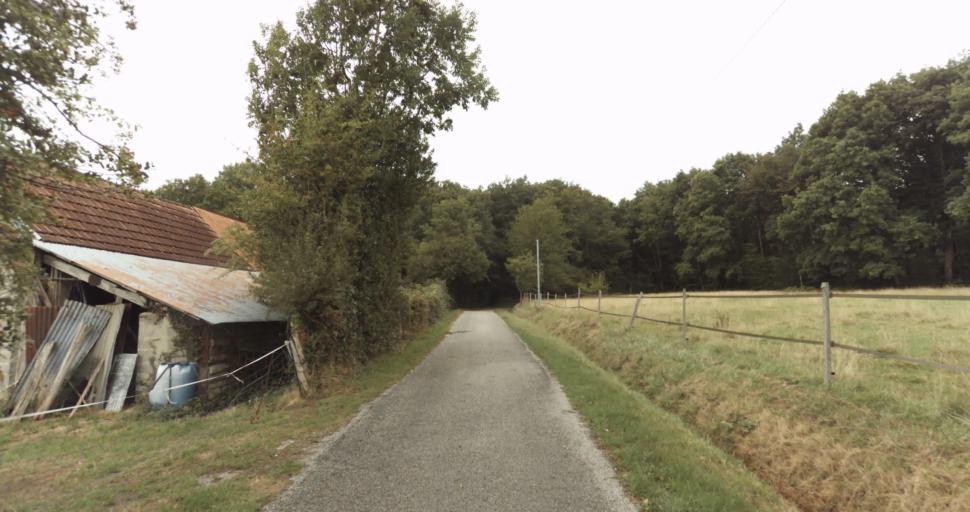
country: FR
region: Lower Normandy
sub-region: Departement de l'Orne
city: Sainte-Gauburge-Sainte-Colombe
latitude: 48.7521
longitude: 0.4730
